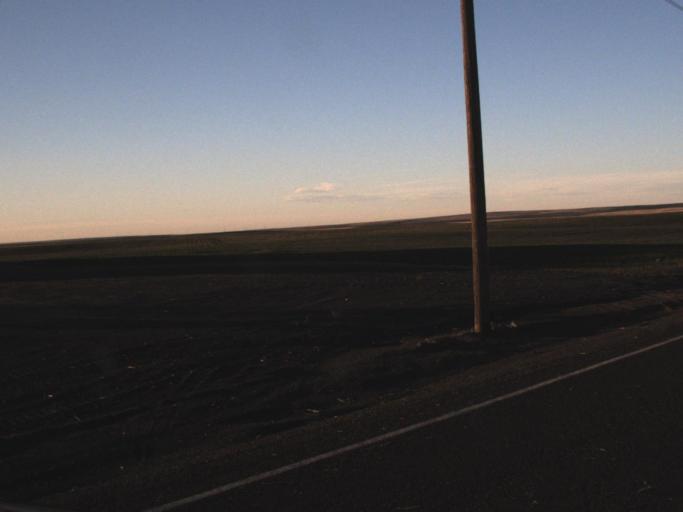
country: US
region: Washington
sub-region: Franklin County
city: Connell
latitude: 46.8110
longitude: -118.5473
